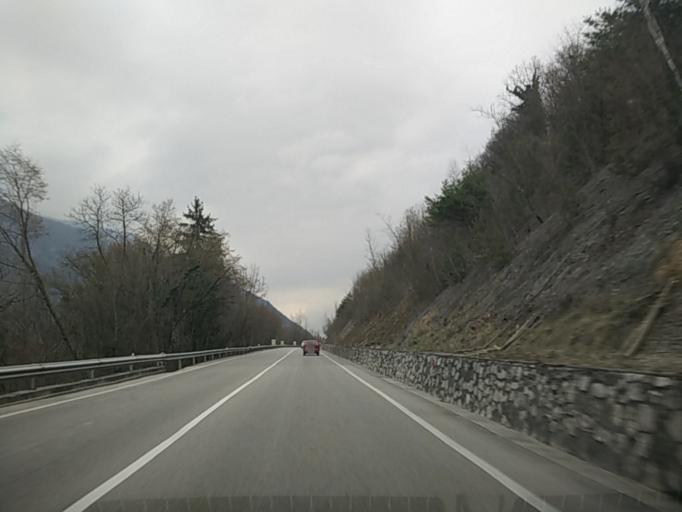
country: IT
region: Veneto
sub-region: Provincia di Belluno
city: Ponte nell'Alpi
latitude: 46.1671
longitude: 12.2704
